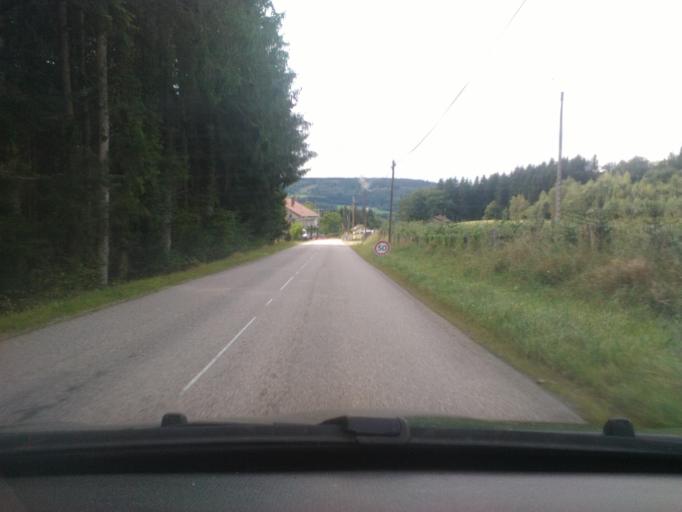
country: FR
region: Lorraine
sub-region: Departement des Vosges
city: Granges-sur-Vologne
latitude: 48.1422
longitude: 6.8233
